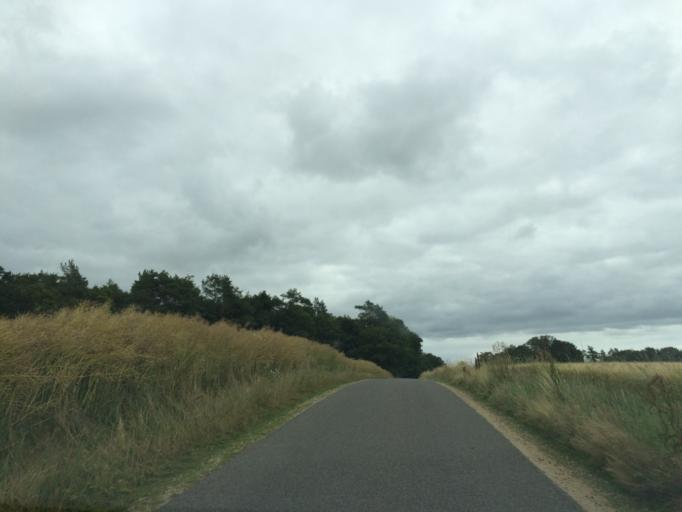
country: DK
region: Central Jutland
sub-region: Silkeborg Kommune
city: Svejbaek
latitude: 56.2060
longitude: 9.6395
